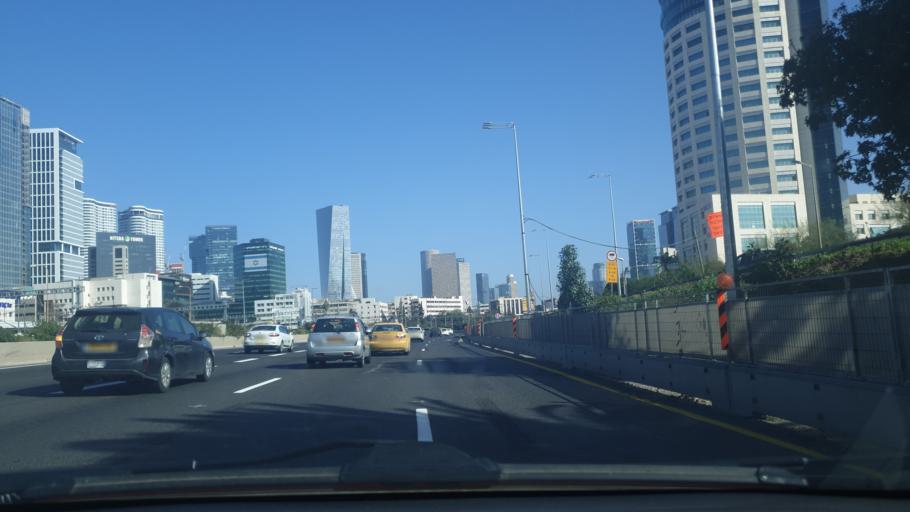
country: IL
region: Tel Aviv
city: Tel Aviv
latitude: 32.0602
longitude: 34.7868
